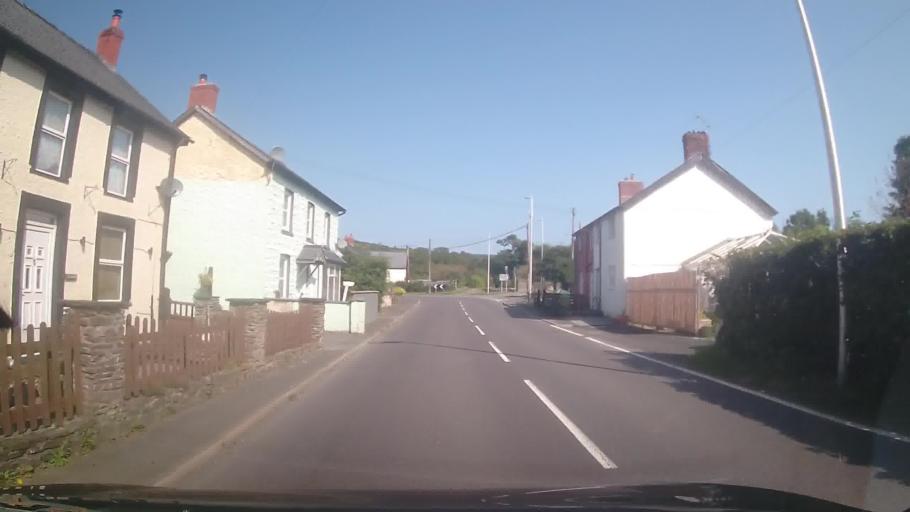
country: GB
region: Wales
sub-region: Sir Powys
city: Rhayader
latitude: 52.1481
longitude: -3.5782
